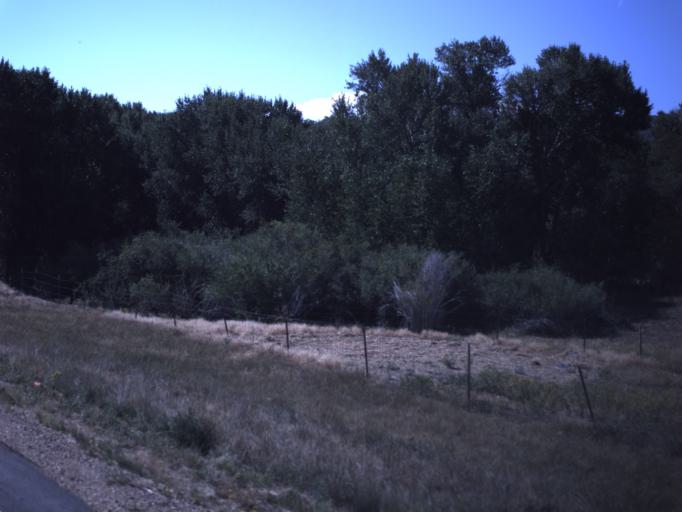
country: US
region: Utah
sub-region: Duchesne County
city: Duchesne
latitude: 40.3645
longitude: -110.7216
